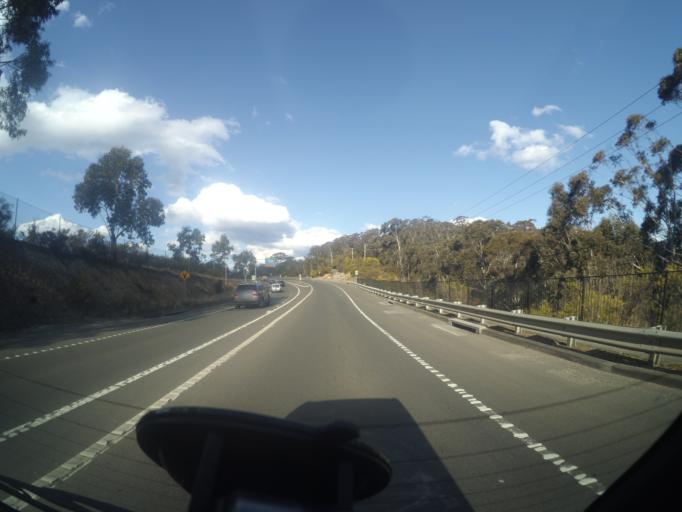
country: AU
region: New South Wales
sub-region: Blue Mountains Municipality
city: Katoomba
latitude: -33.7059
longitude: 150.2942
